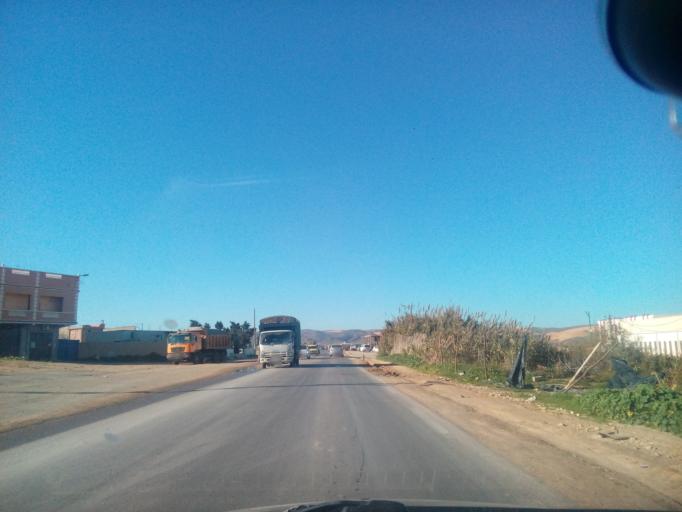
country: DZ
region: Relizane
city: Relizane
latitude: 35.9106
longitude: 0.5053
